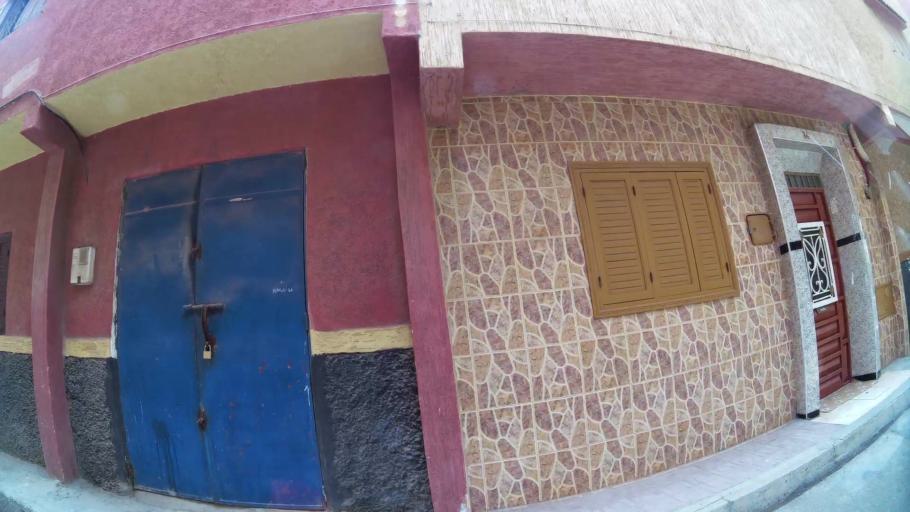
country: MA
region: Rabat-Sale-Zemmour-Zaer
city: Sale
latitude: 34.0559
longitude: -6.7857
